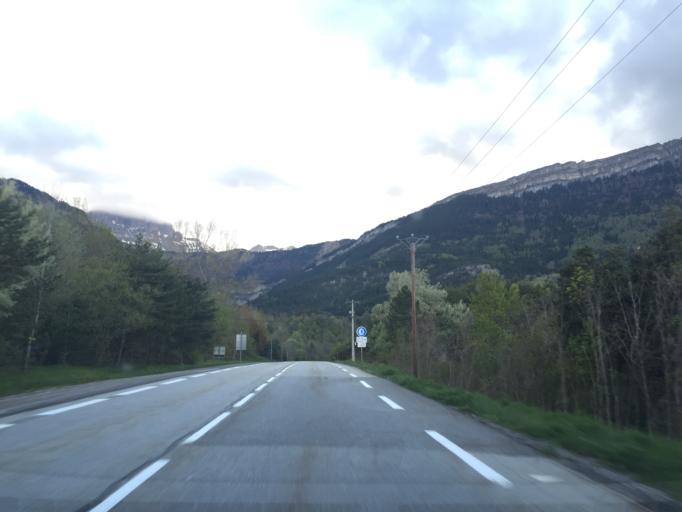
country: FR
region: Rhone-Alpes
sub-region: Departement de l'Isere
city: La Motte-Saint-Martin
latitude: 44.8607
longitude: 5.6042
